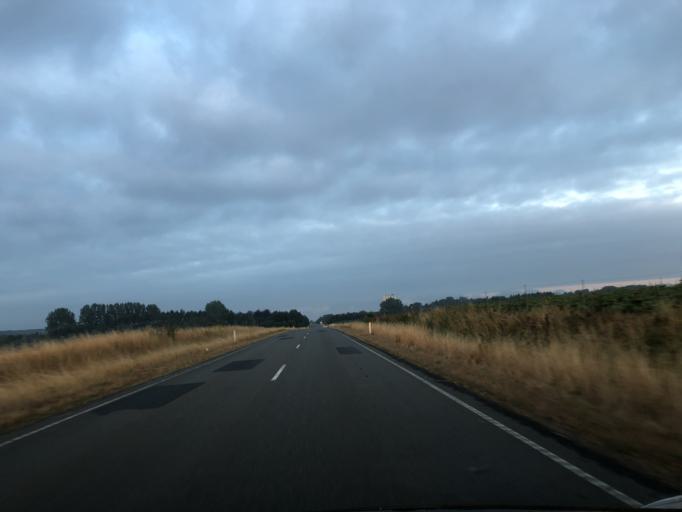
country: DK
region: Zealand
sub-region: Soro Kommune
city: Dianalund
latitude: 55.5016
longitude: 11.5229
